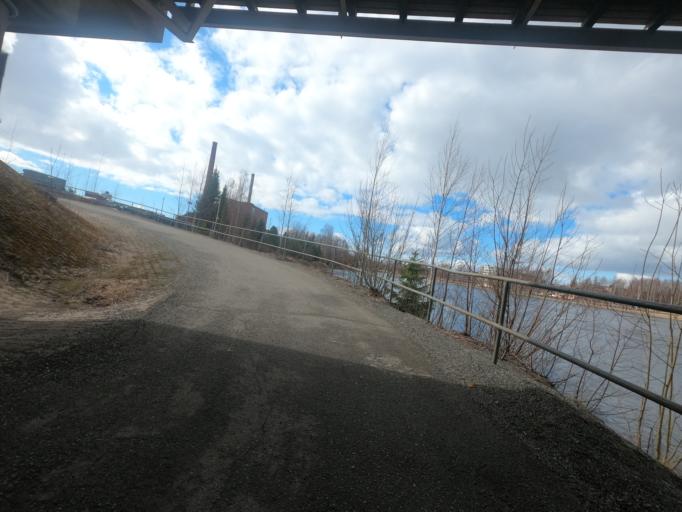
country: FI
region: North Karelia
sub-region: Joensuu
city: Joensuu
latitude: 62.6059
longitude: 29.7799
